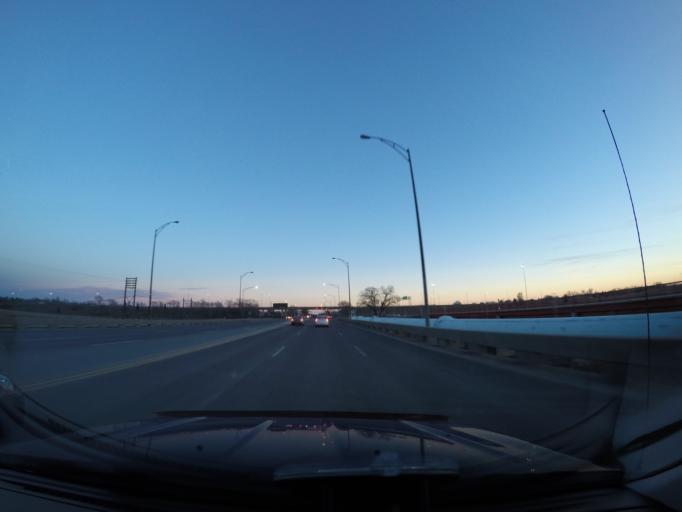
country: US
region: Kansas
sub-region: Sedgwick County
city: Wichita
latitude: 37.7158
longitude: -97.4018
